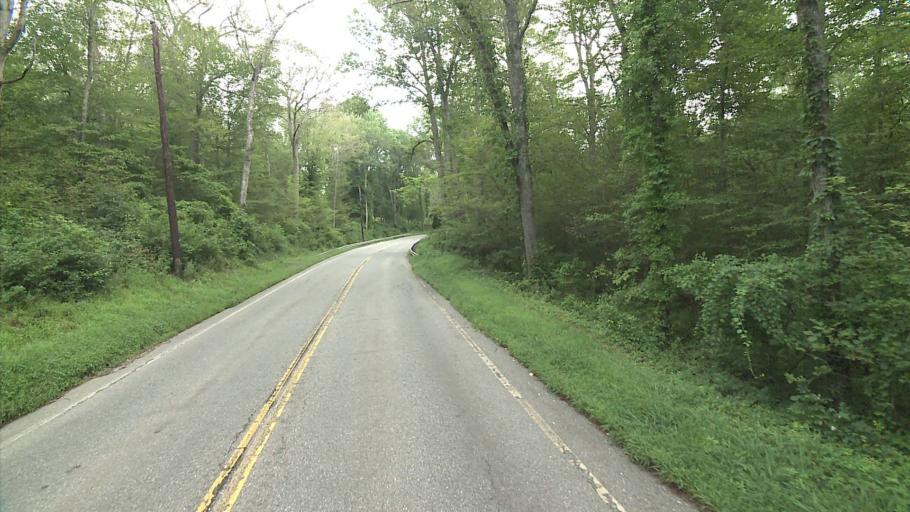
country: US
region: Connecticut
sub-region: New London County
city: Colchester
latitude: 41.4576
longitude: -72.3033
